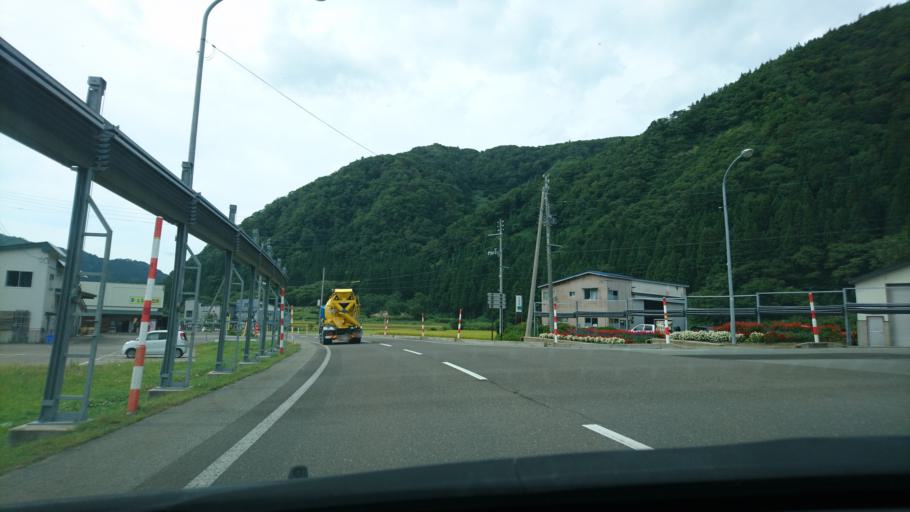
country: JP
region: Akita
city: Yuzawa
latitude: 39.1752
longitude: 140.6916
